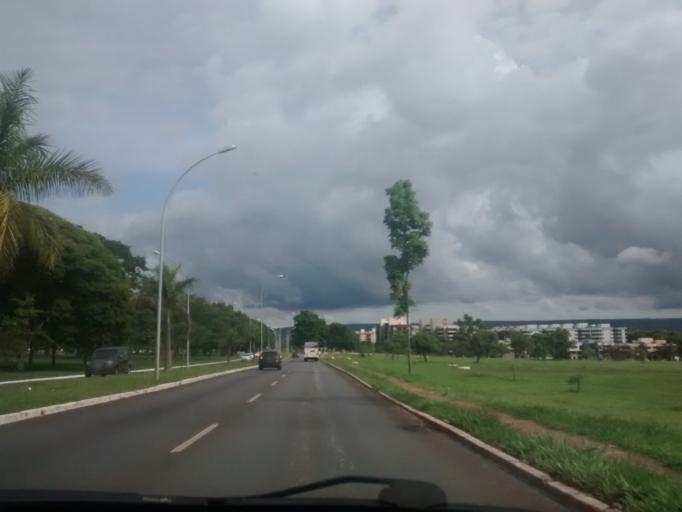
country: BR
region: Federal District
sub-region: Brasilia
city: Brasilia
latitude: -15.7676
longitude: -47.8817
